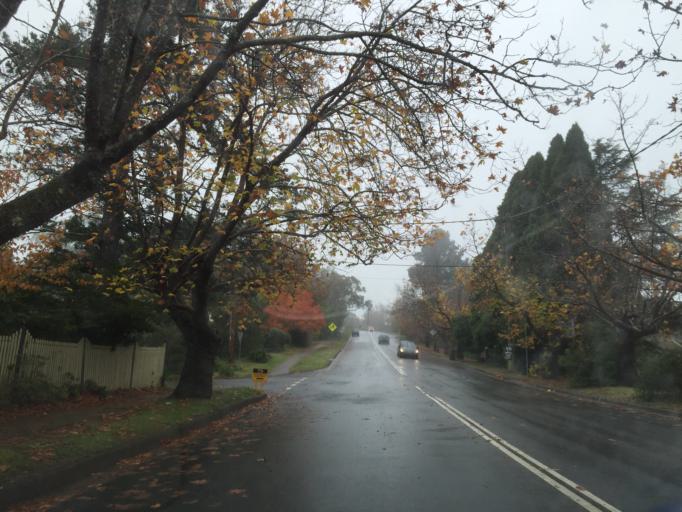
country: AU
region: New South Wales
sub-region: Blue Mountains Municipality
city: Leura
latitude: -33.7070
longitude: 150.3760
